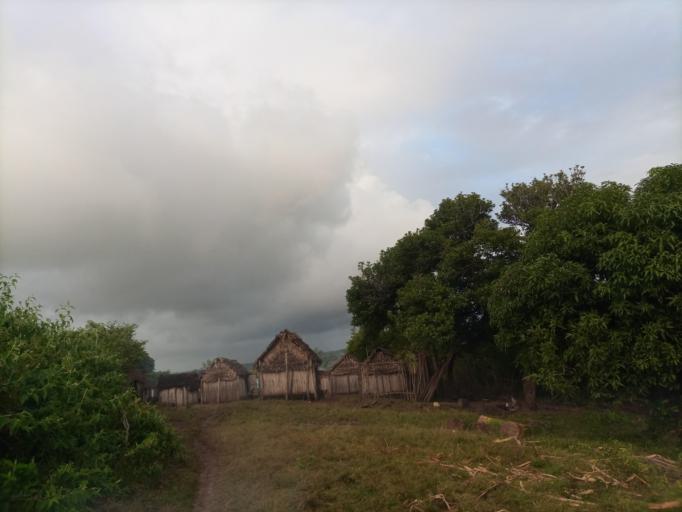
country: MG
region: Anosy
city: Fort Dauphin
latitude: -24.7032
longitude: 47.1777
